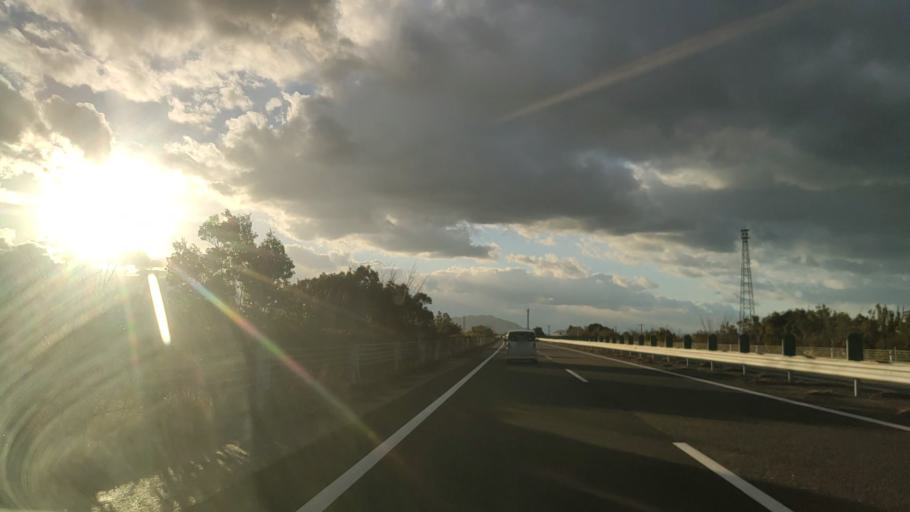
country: JP
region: Ehime
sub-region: Shikoku-chuo Shi
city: Matsuyama
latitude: 33.7858
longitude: 132.8628
